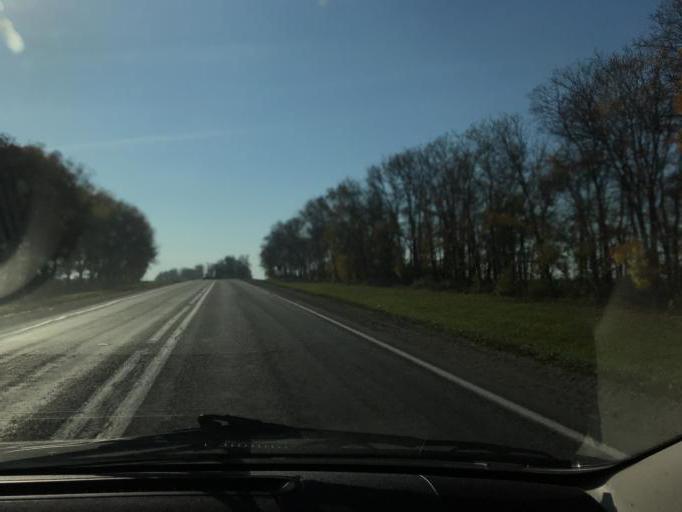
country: BY
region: Minsk
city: Salihorsk
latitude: 52.8802
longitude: 27.4682
